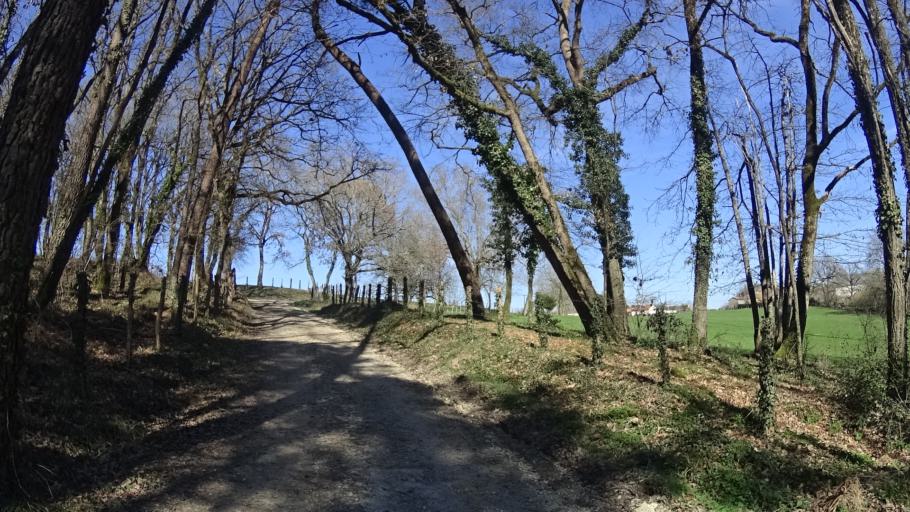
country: FR
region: Aquitaine
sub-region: Departement de la Dordogne
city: Riberac
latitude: 45.2151
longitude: 0.3284
